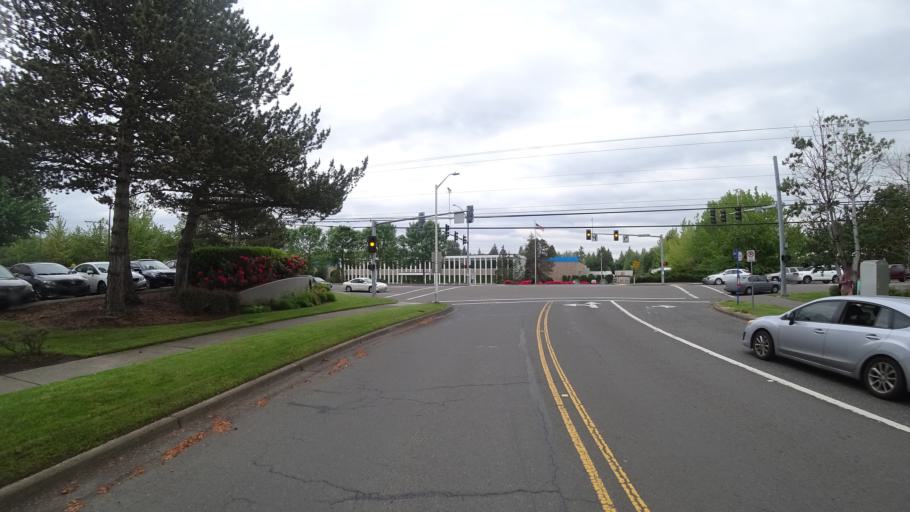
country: US
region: Oregon
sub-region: Washington County
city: Raleigh Hills
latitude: 45.4749
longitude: -122.7787
